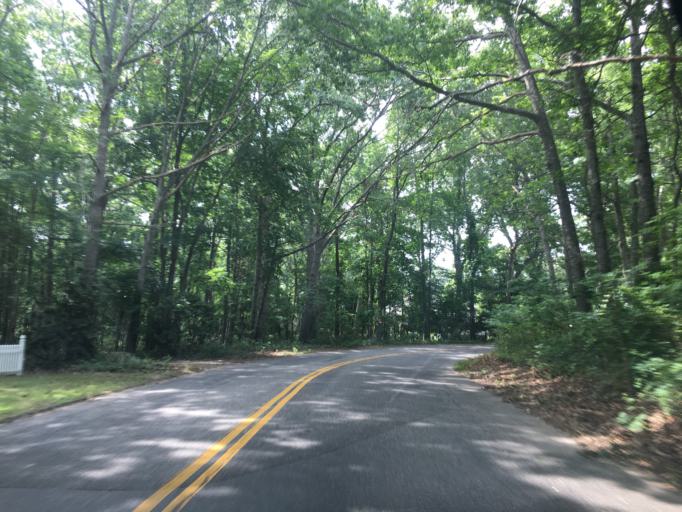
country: US
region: New York
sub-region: Suffolk County
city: Shelter Island Heights
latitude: 41.0965
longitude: -72.3315
